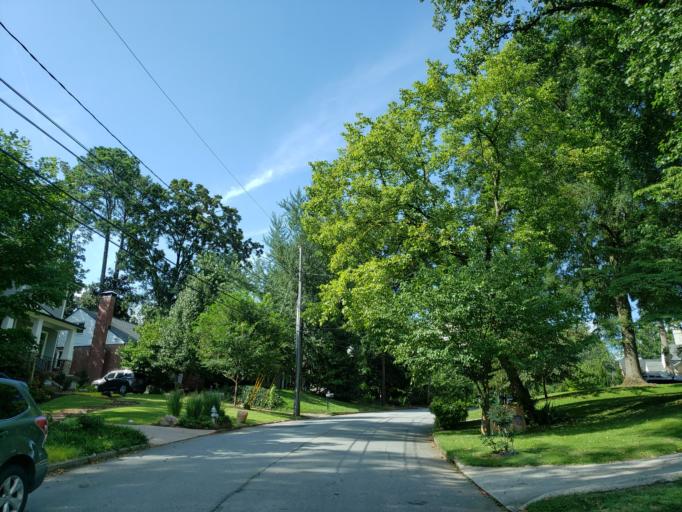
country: US
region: Georgia
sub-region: DeKalb County
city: Druid Hills
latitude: 33.7909
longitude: -84.3636
